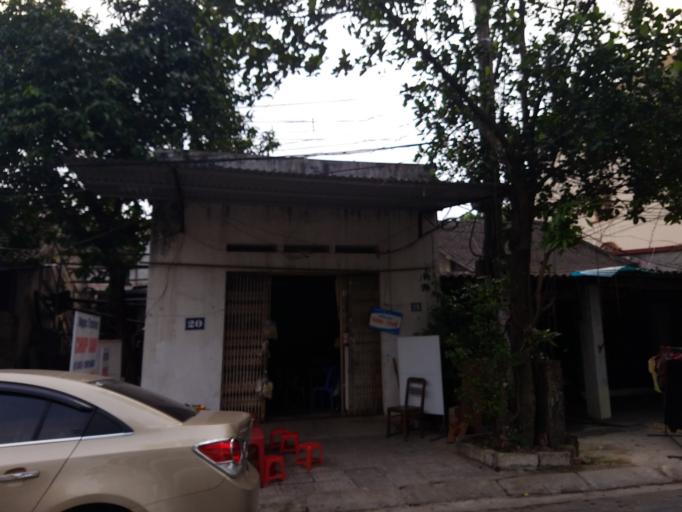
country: VN
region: Thai Nguyen
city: Thanh Pho Thai Nguyen
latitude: 21.5935
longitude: 105.8429
